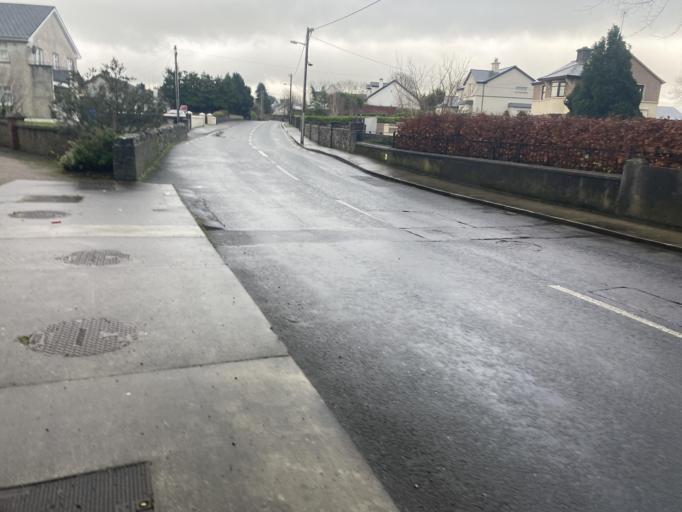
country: IE
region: Connaught
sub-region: County Galway
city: Tuam
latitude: 53.5187
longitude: -8.8422
